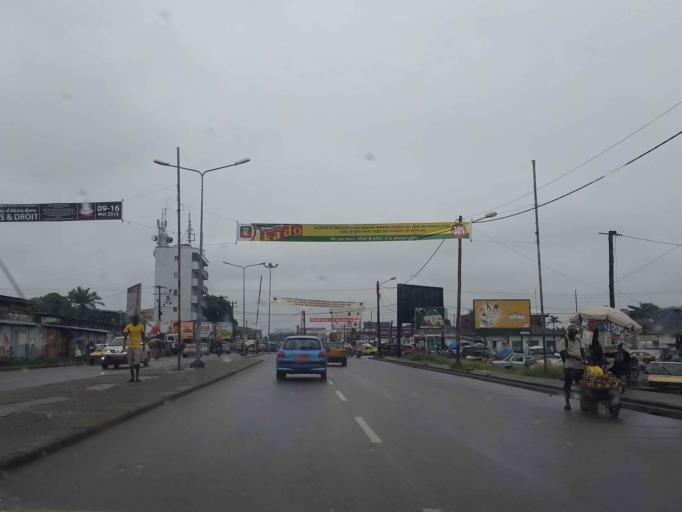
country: CM
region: Littoral
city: Douala
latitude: 4.0656
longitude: 9.7150
